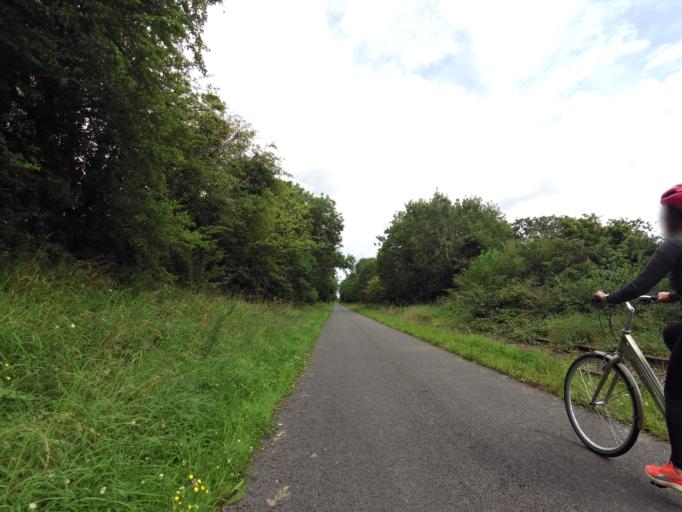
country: IE
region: Leinster
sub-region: An Iarmhi
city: Kilbeggan
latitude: 53.4829
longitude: -7.4690
